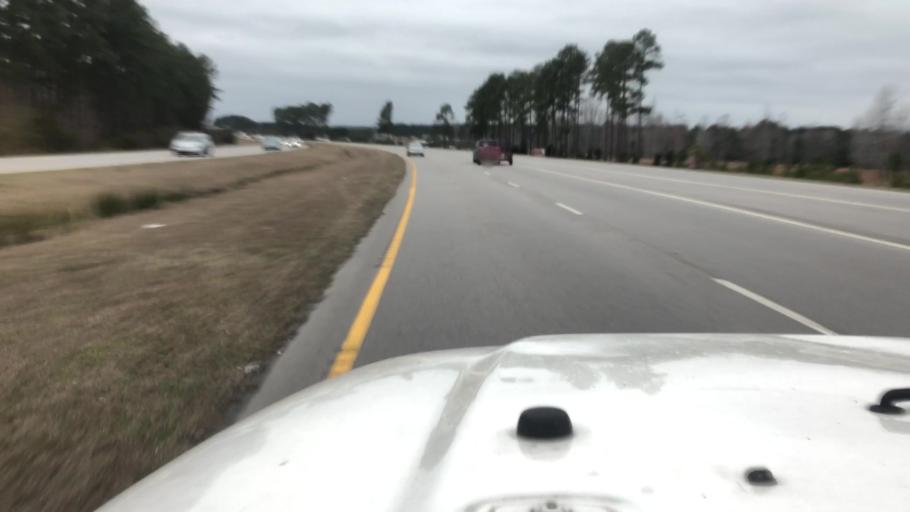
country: US
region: South Carolina
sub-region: Beaufort County
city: Bluffton
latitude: 32.2965
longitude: -80.9405
